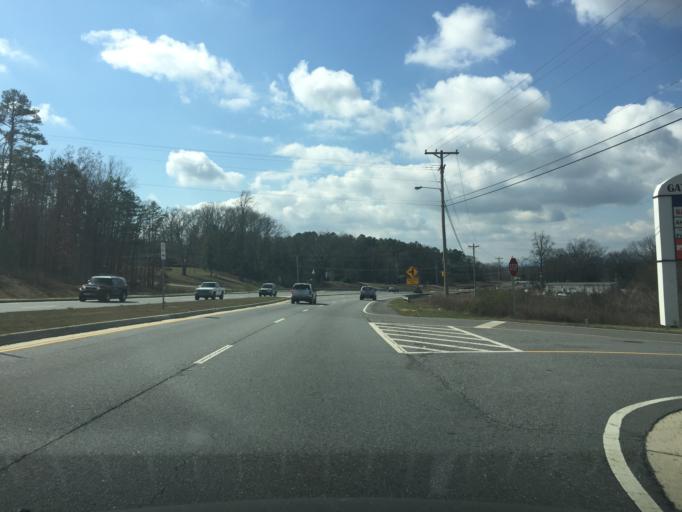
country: US
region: Georgia
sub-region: Catoosa County
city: Indian Springs
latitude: 34.9605
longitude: -85.1958
